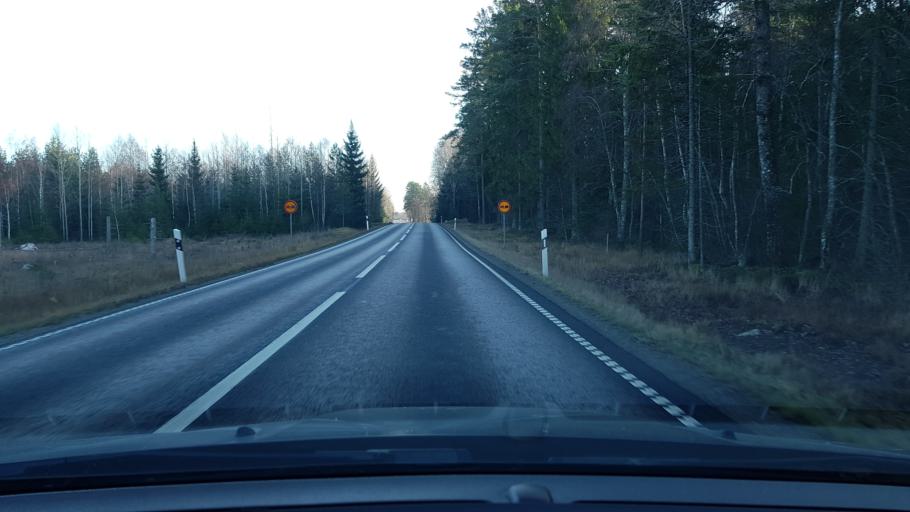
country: SE
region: Stockholm
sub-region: Norrtalje Kommun
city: Nykvarn
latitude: 59.7405
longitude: 18.2293
